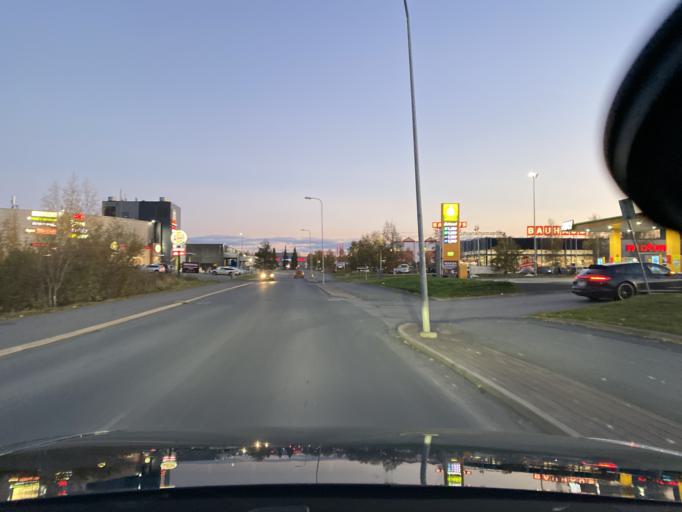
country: FI
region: Pirkanmaa
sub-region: Tampere
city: Tampere
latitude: 61.4687
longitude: 23.7179
